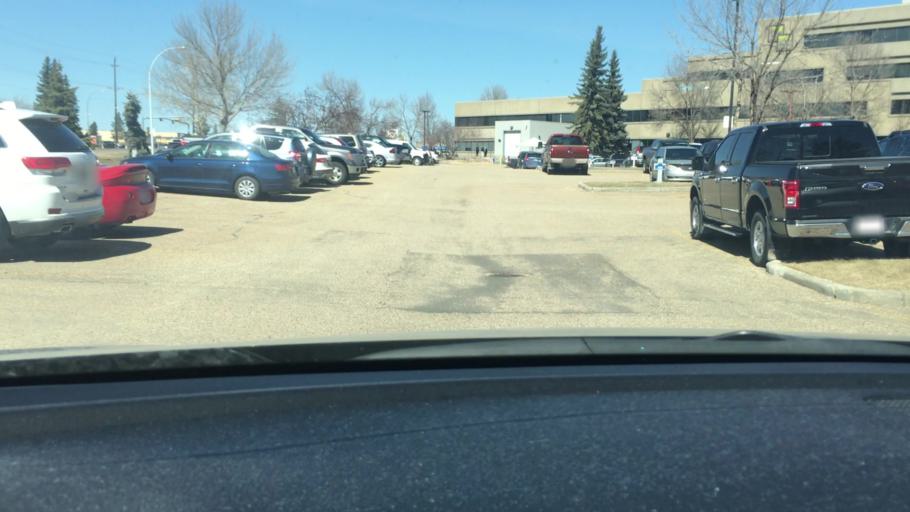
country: CA
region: Alberta
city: Edmonton
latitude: 53.5356
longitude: -113.4178
